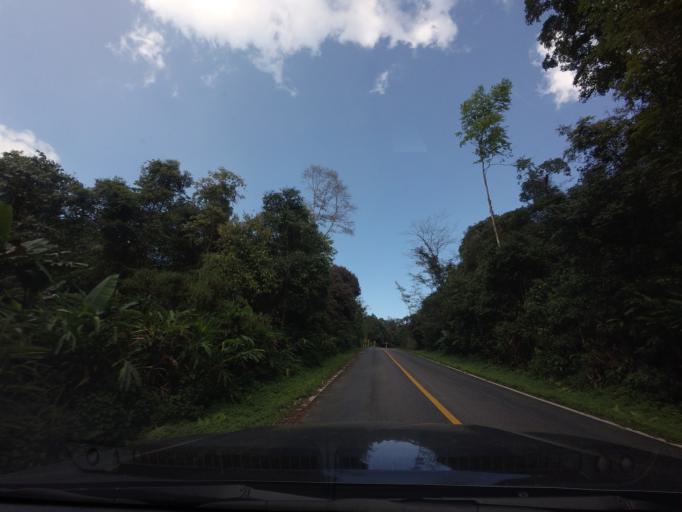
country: TH
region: Phetchabun
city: Lom Kao
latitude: 16.9486
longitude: 101.0278
